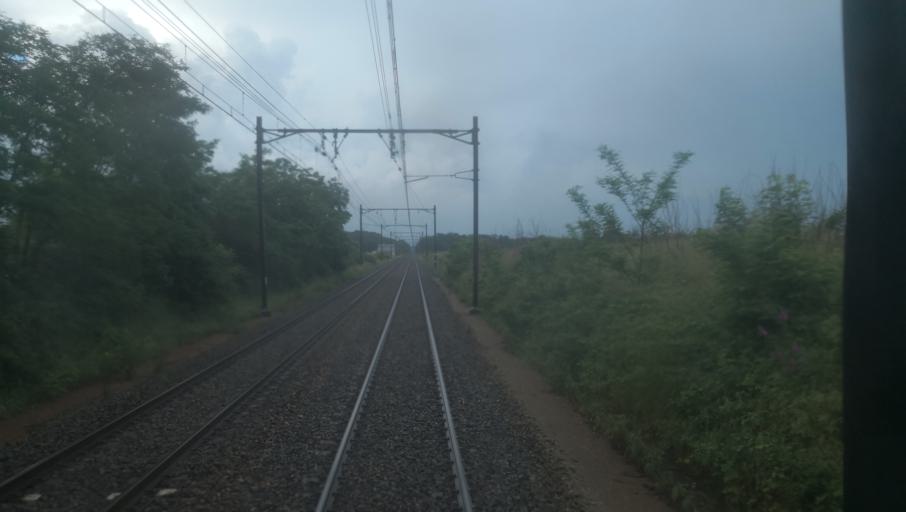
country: FR
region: Centre
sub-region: Departement du Loiret
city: Saint-Cyr-en-Val
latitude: 47.7988
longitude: 1.9436
